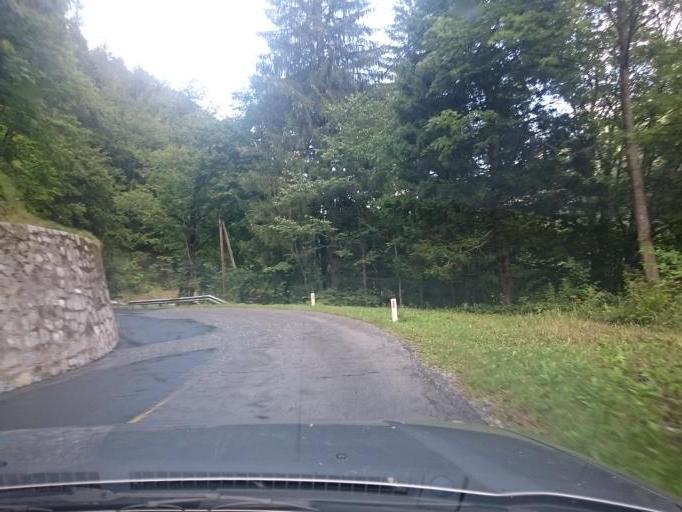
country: AT
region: Carinthia
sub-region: Politischer Bezirk Spittal an der Drau
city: Oberdrauburg
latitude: 46.6373
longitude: 12.9567
